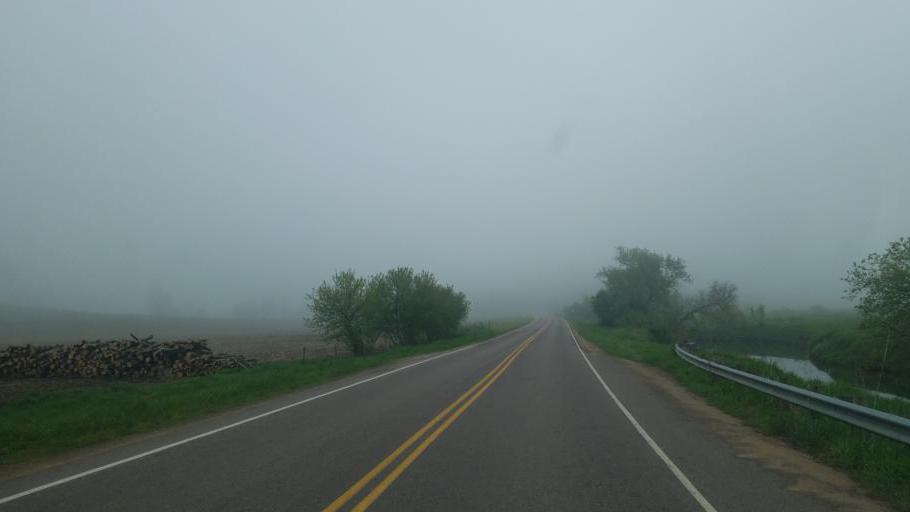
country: US
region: Wisconsin
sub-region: Vernon County
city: Hillsboro
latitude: 43.6380
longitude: -90.3525
